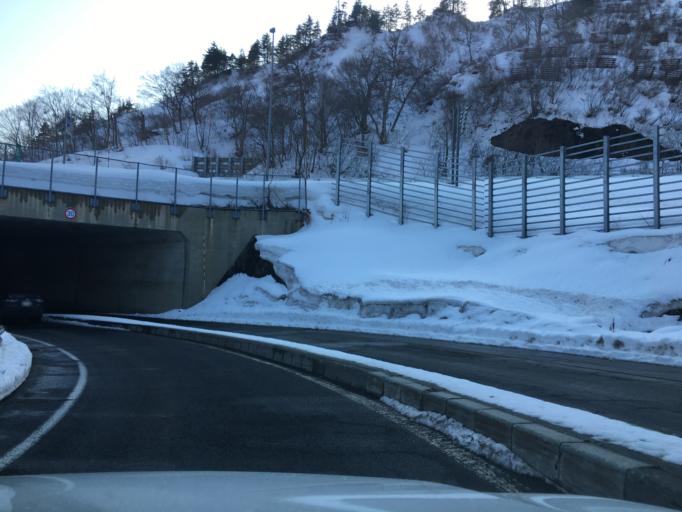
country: JP
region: Yamagata
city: Sagae
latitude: 38.4562
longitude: 139.9923
